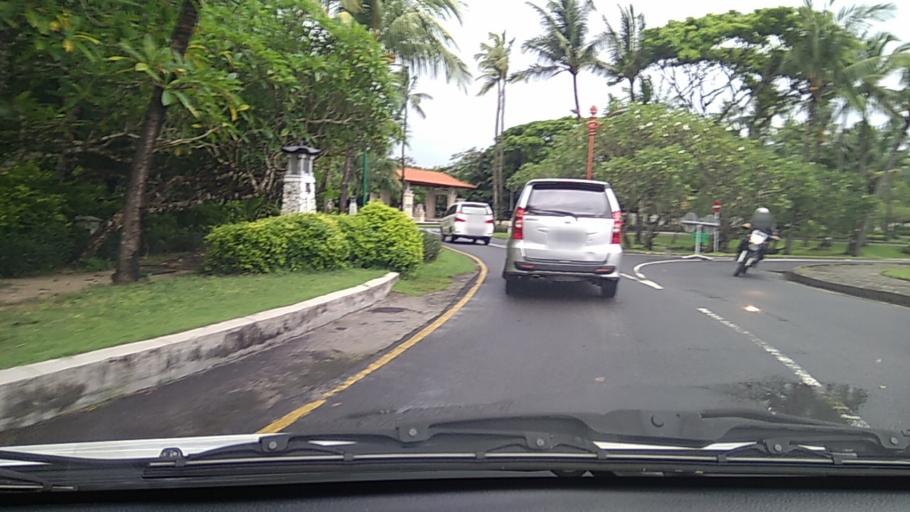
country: ID
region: Bali
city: Bualu
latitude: -8.8025
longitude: 115.2314
